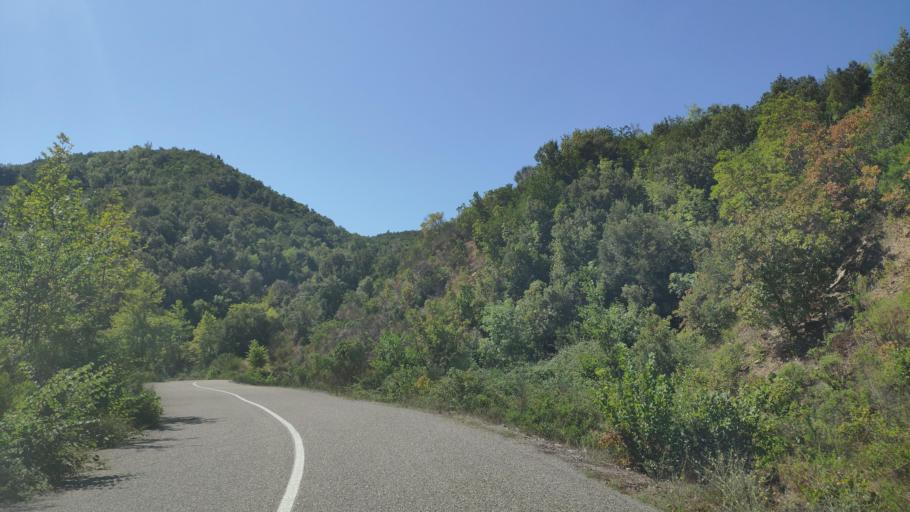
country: GR
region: Central Greece
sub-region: Nomos Evrytanias
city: Kerasochori
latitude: 39.0031
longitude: 21.5400
